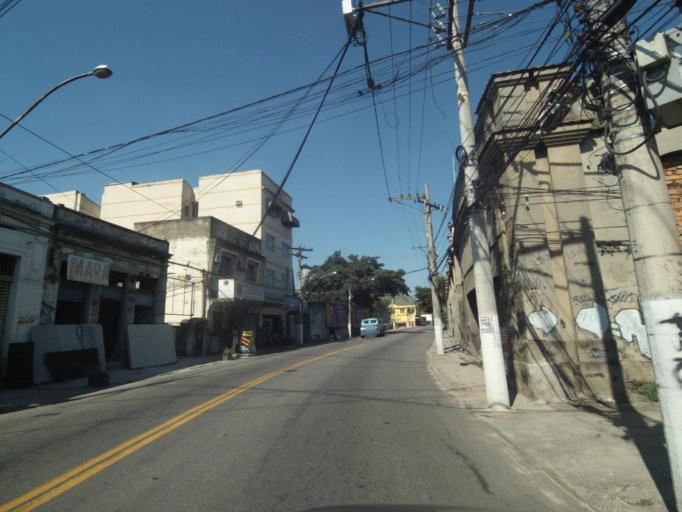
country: BR
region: Rio de Janeiro
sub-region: Niteroi
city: Niteroi
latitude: -22.8598
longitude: -43.0997
